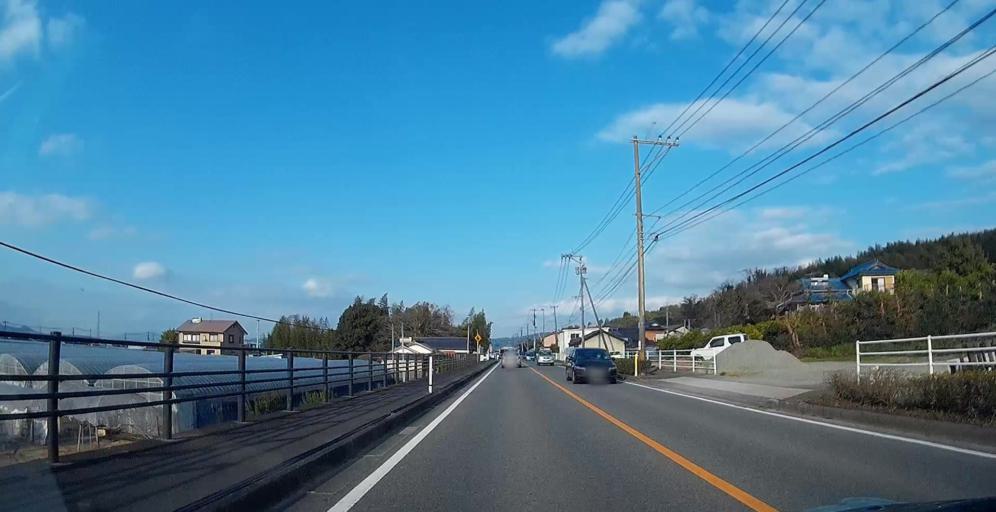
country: JP
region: Kumamoto
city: Matsubase
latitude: 32.5690
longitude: 130.6904
